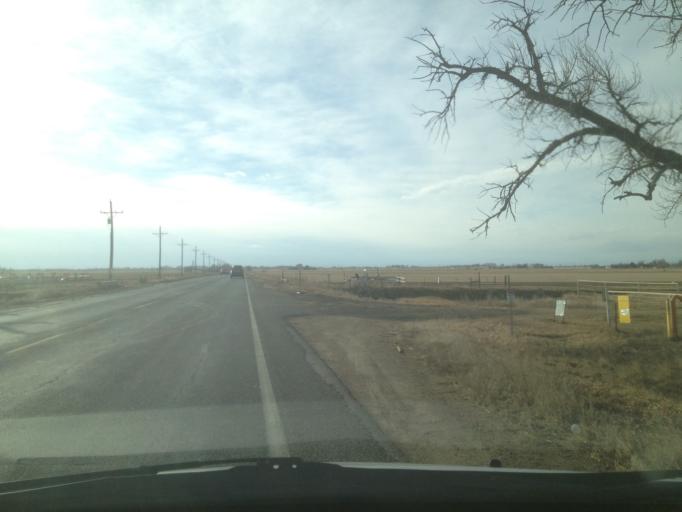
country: US
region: Colorado
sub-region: Weld County
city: Hudson
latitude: 40.0806
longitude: -104.6665
